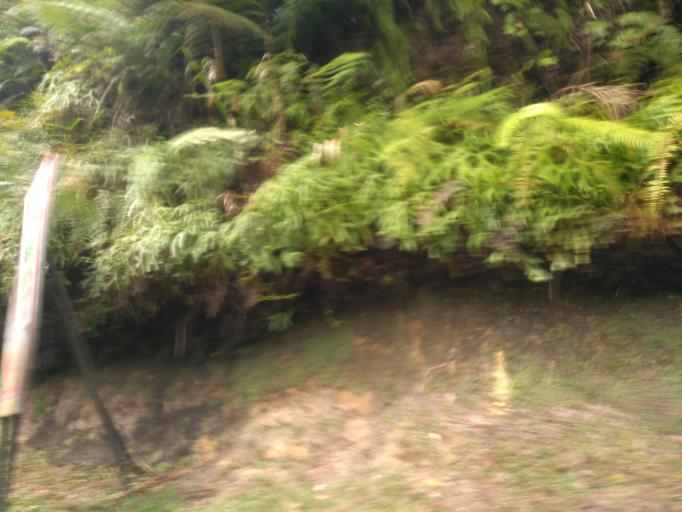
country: MY
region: Pahang
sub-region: Cameron Highlands
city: Tanah Rata
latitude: 4.4666
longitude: 101.3675
